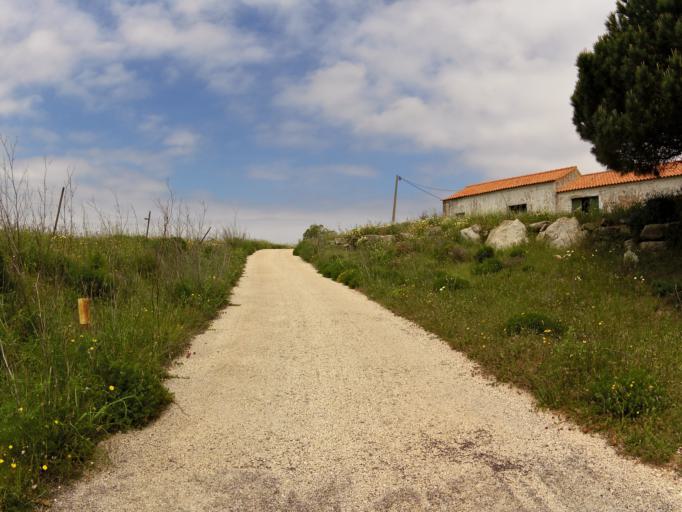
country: PT
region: Faro
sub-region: Vila do Bispo
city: Vila do Bispo
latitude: 37.0787
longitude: -8.8789
